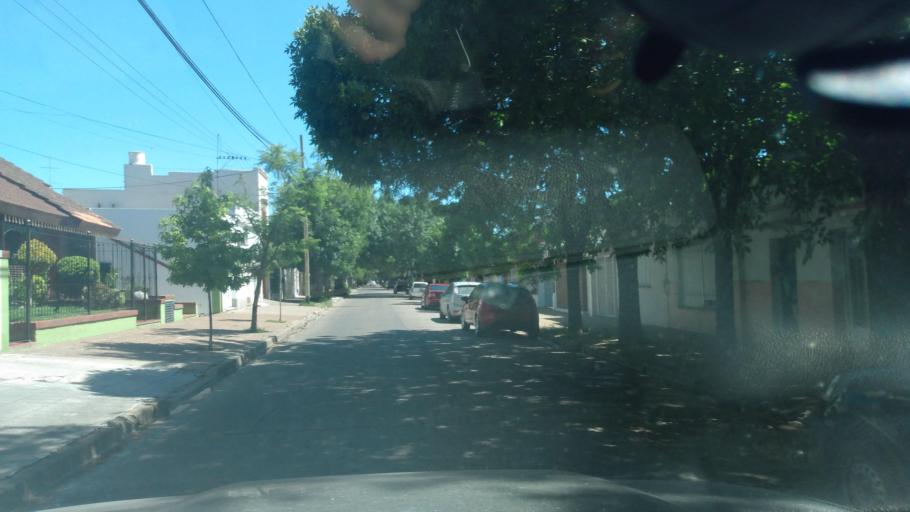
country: AR
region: Buenos Aires
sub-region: Partido de Lujan
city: Lujan
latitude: -34.5674
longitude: -59.1061
